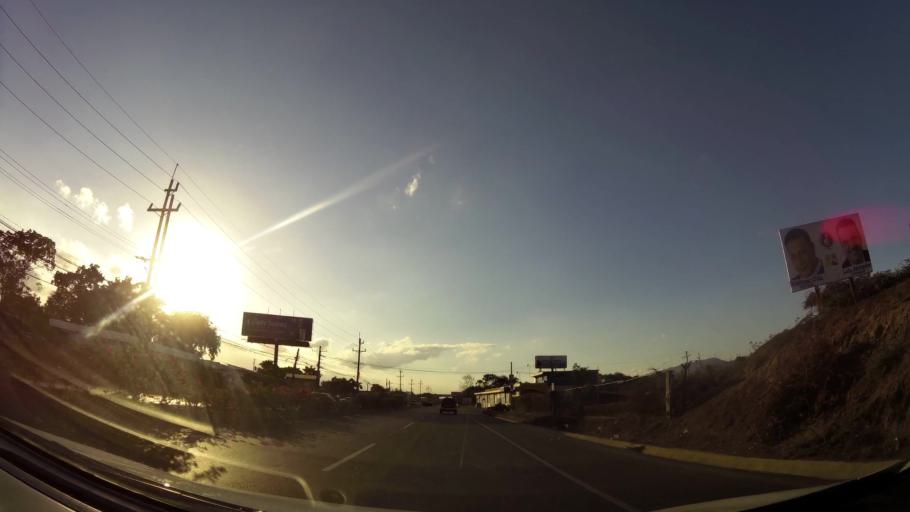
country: DO
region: Santiago
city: Palmar Arriba
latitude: 19.5004
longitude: -70.7433
